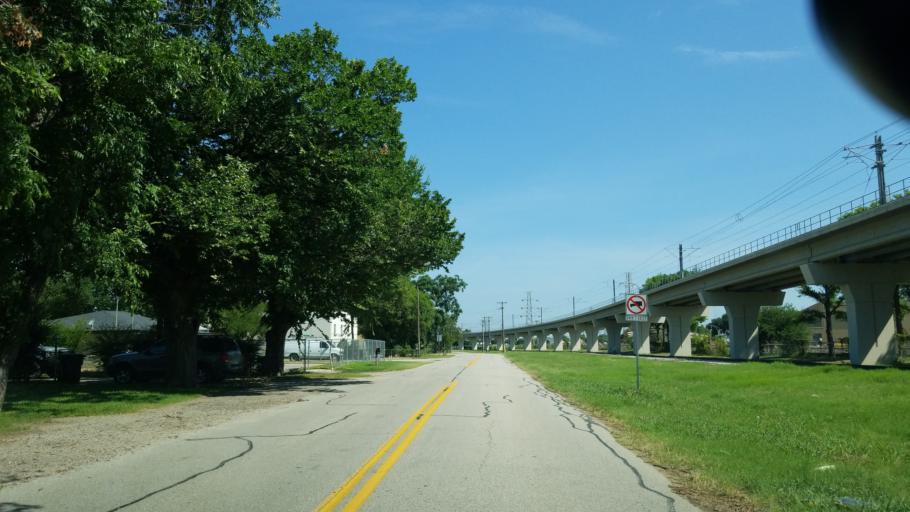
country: US
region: Texas
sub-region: Dallas County
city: Carrollton
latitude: 32.9691
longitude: -96.9171
